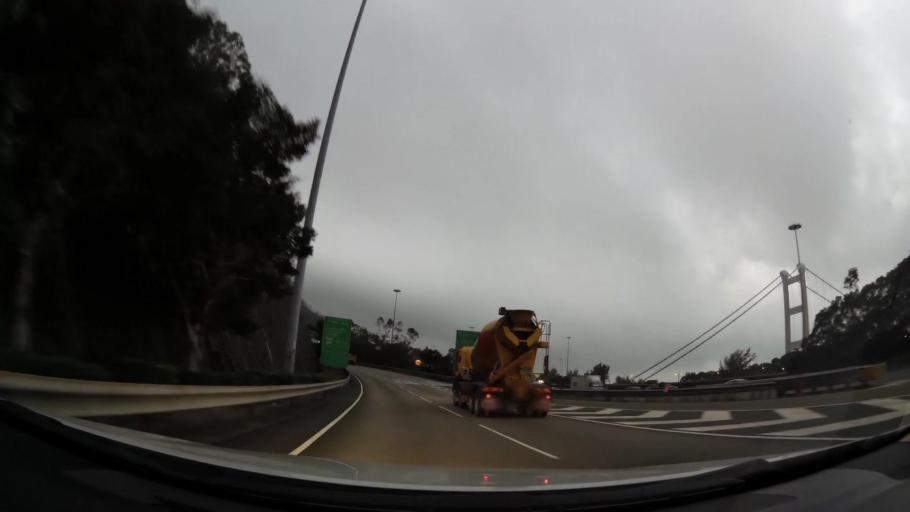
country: HK
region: Tsuen Wan
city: Tsuen Wan
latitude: 22.3575
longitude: 114.0836
